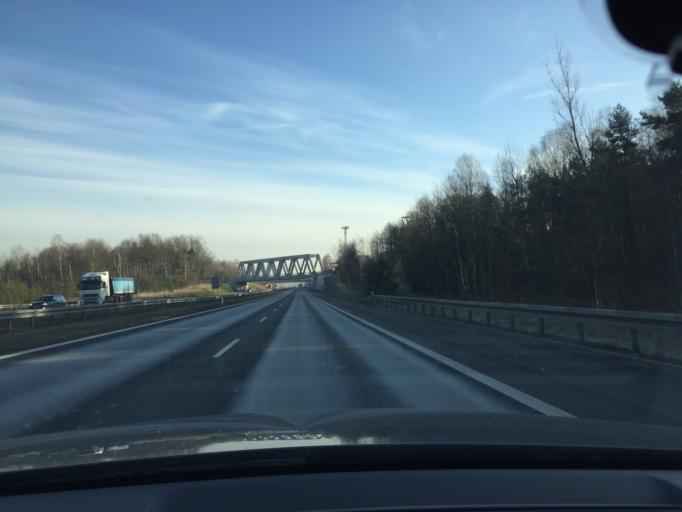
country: PL
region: Silesian Voivodeship
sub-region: Katowice
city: Murcki
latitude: 50.2297
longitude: 19.0706
